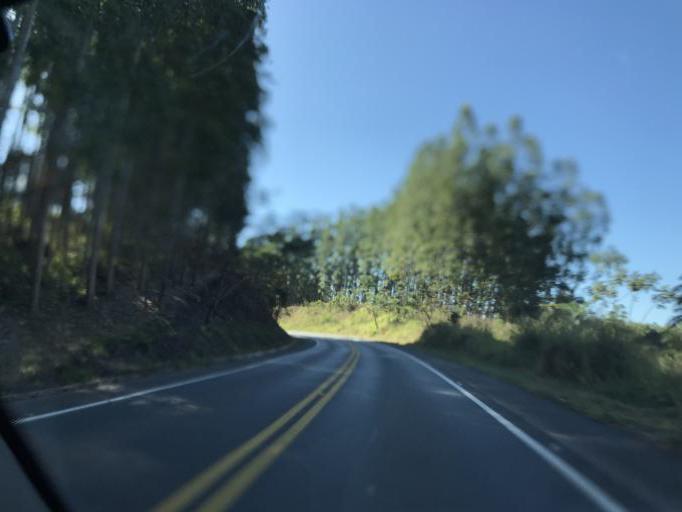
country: BR
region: Minas Gerais
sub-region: Bambui
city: Bambui
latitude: -19.8267
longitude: -46.0096
